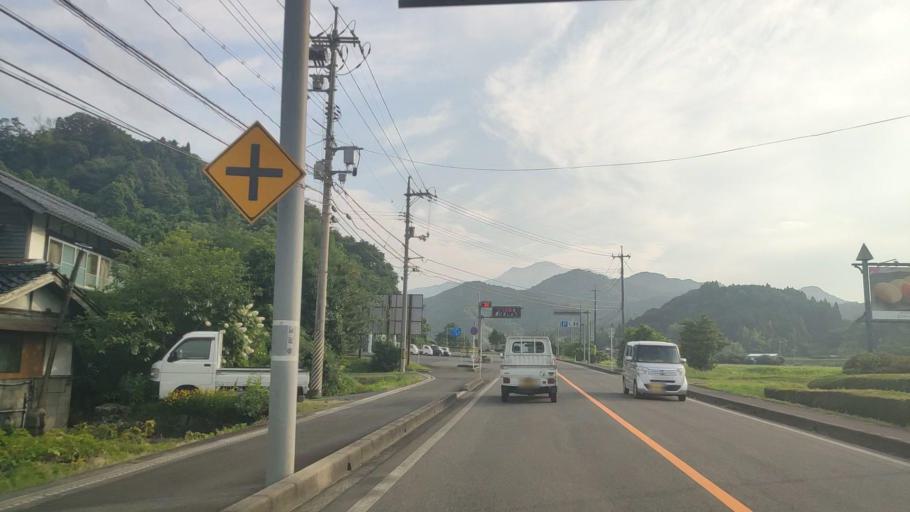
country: JP
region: Tottori
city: Kurayoshi
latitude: 35.3624
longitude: 133.7535
